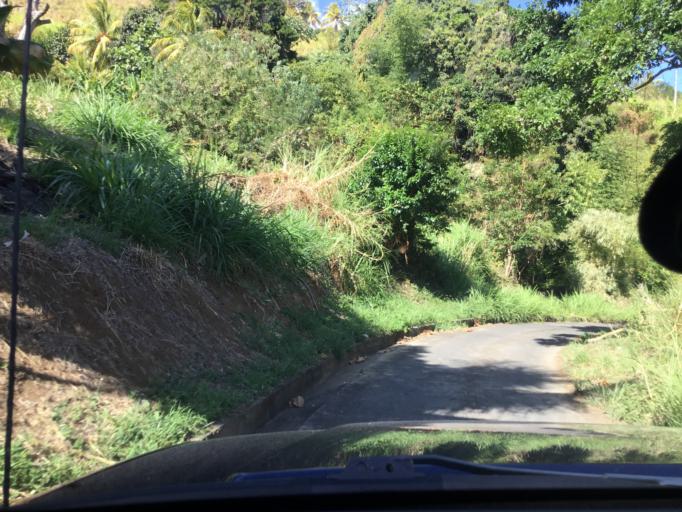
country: VC
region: Charlotte
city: Biabou
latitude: 13.1613
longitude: -61.1665
